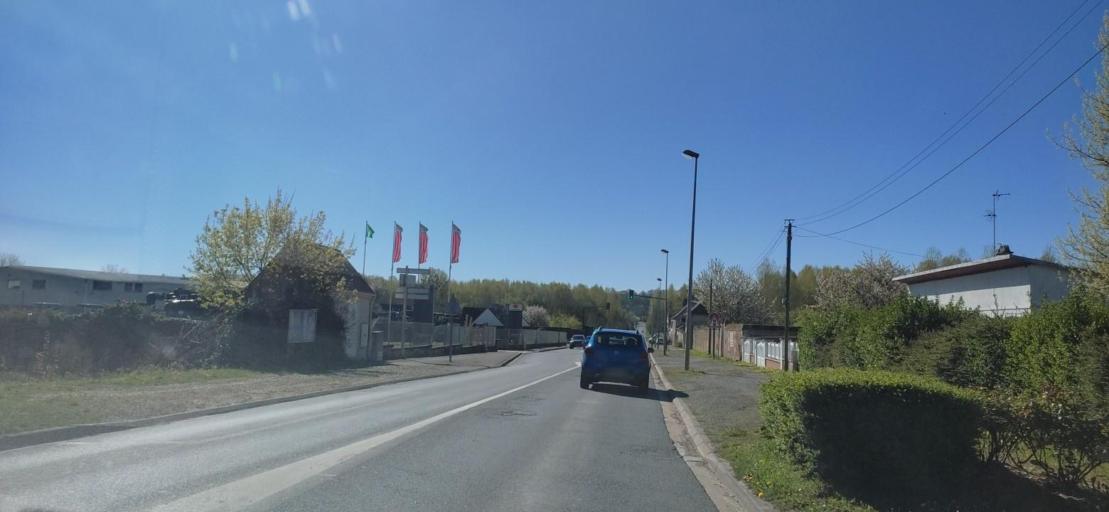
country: FR
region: Picardie
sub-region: Departement de l'Oise
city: Villers-sur-Coudun
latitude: 49.4701
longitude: 2.7567
